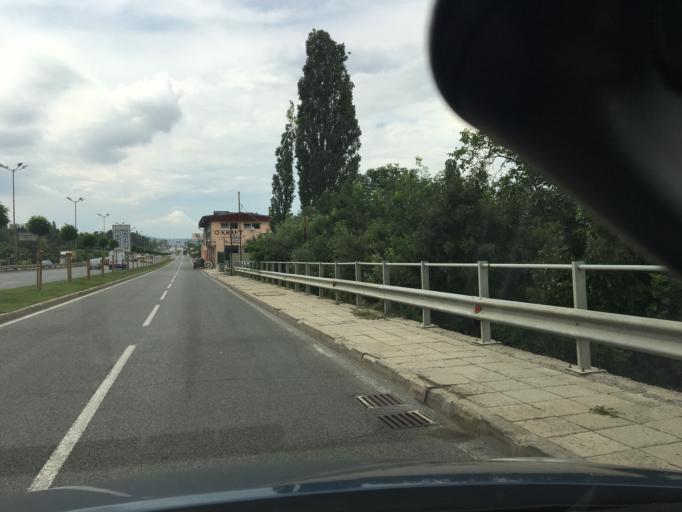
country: BG
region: Sofia-Capital
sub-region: Stolichna Obshtina
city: Sofia
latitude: 42.6441
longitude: 23.3070
